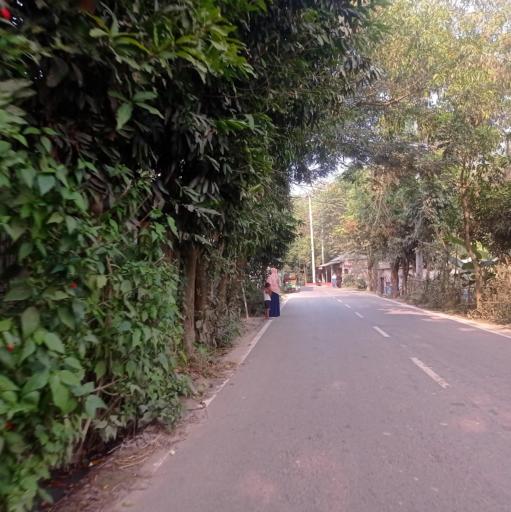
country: BD
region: Dhaka
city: Bhairab Bazar
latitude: 24.0955
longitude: 90.8527
